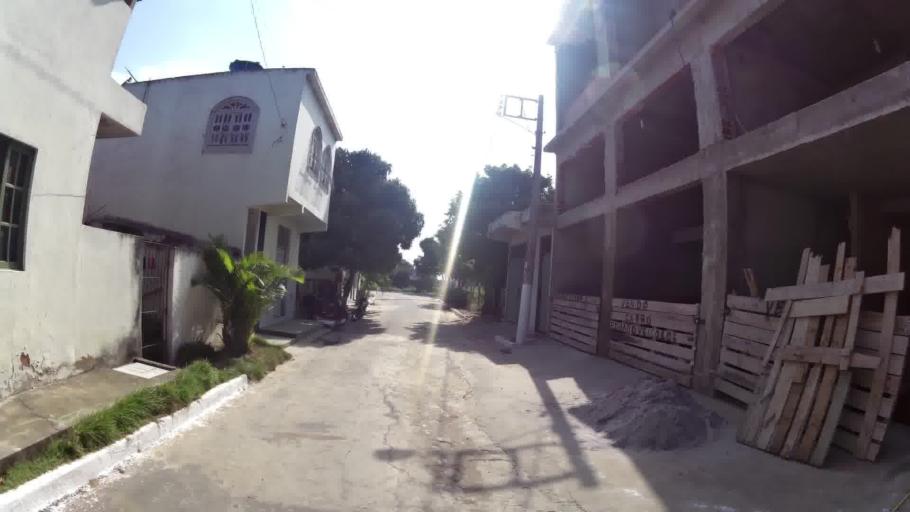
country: BR
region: Espirito Santo
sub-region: Itapemirim
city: Itapemirim
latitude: -21.0063
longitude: -40.8343
